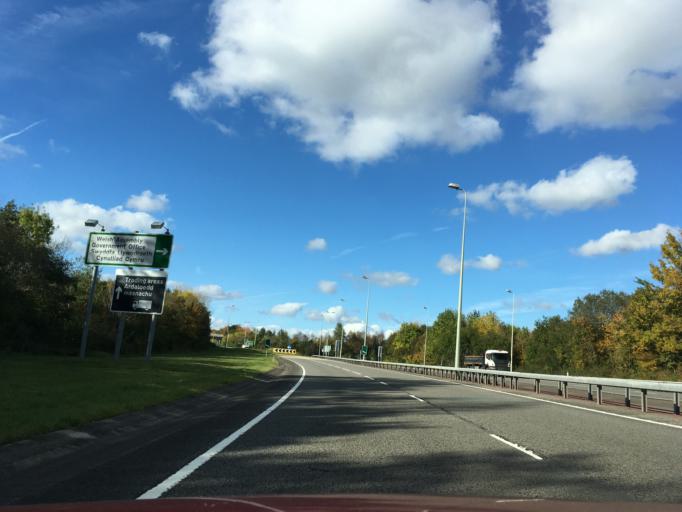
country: GB
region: Wales
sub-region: Merthyr Tydfil County Borough
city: Merthyr Tydfil
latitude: 51.7352
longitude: -3.3776
